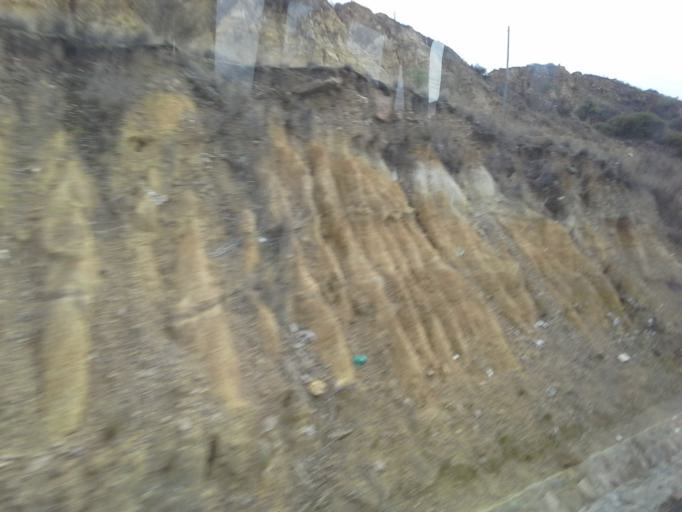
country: BO
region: Cochabamba
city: Colomi
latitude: -17.4099
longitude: -65.9670
